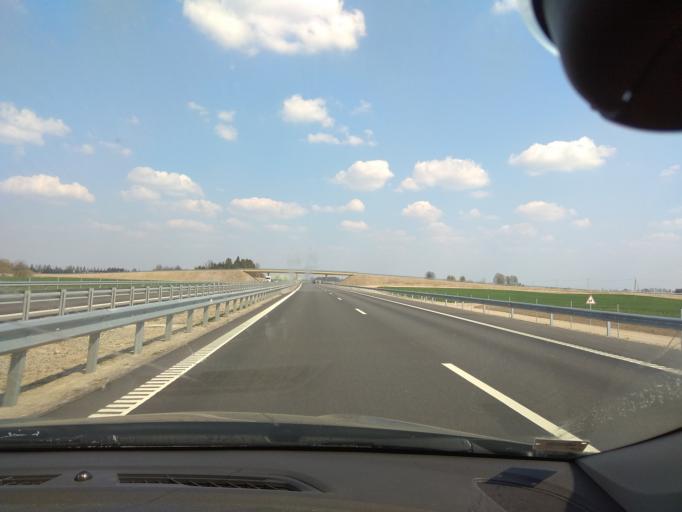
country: LT
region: Kauno apskritis
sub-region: Kauno rajonas
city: Mastaiciai
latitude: 54.7470
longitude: 23.7240
